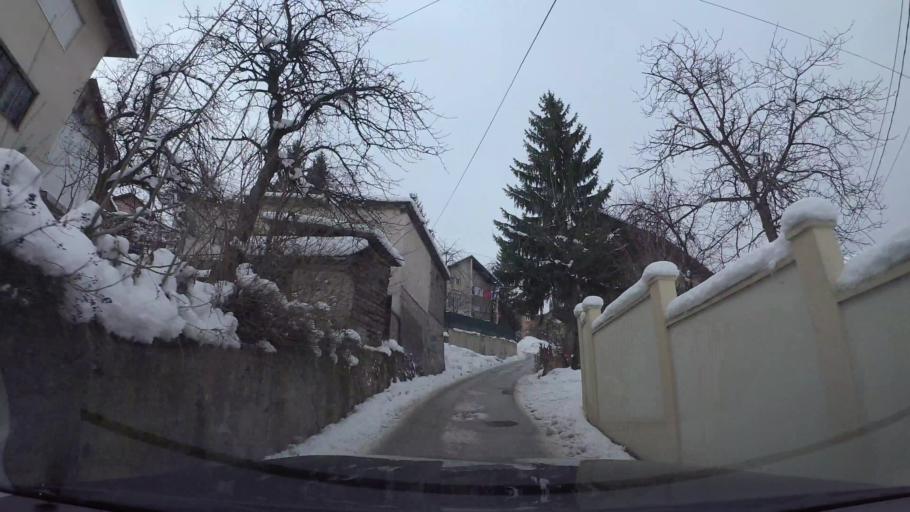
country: BA
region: Federation of Bosnia and Herzegovina
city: Kobilja Glava
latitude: 43.8697
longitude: 18.3985
